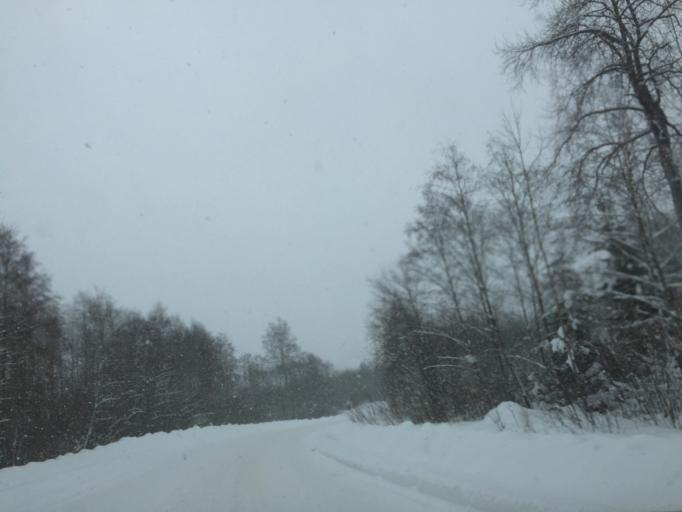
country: LV
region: Amatas Novads
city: Drabesi
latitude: 57.0831
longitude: 25.3471
